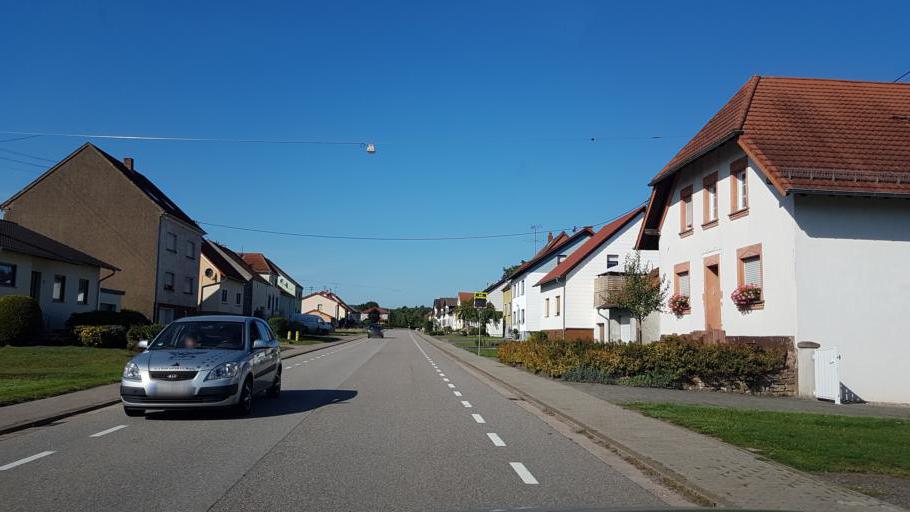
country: DE
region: Saarland
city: Weiskirchen
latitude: 49.5321
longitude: 6.8328
